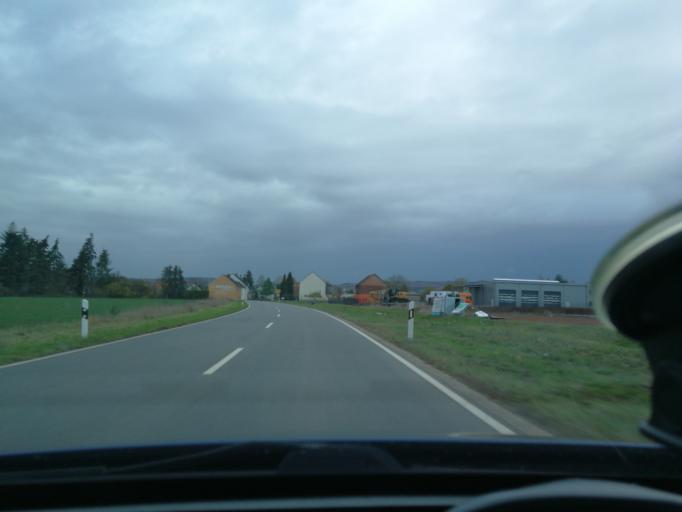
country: DE
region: Rheinland-Pfalz
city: Platten
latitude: 49.9671
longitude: 6.9417
